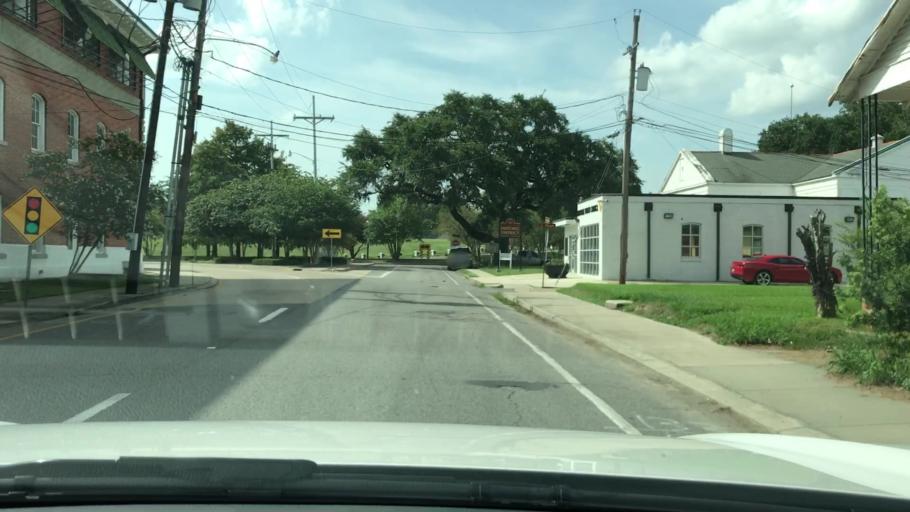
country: US
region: Louisiana
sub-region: Iberville Parish
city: Plaquemine
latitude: 30.2912
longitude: -91.2340
